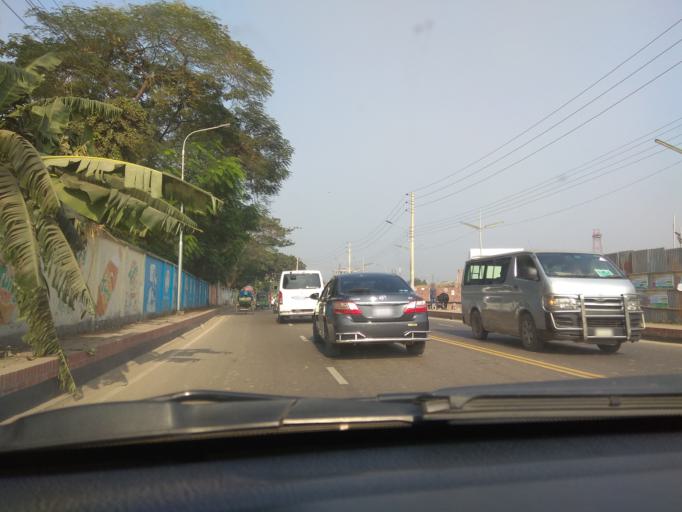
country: BD
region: Dhaka
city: Azimpur
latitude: 23.7690
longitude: 90.3746
